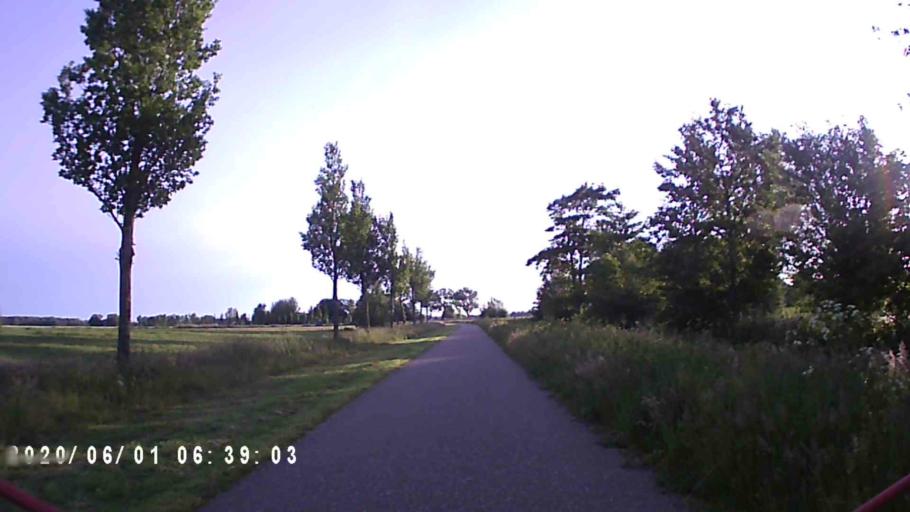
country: NL
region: Friesland
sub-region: Gemeente Kollumerland en Nieuwkruisland
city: Kollum
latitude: 53.2886
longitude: 6.1583
